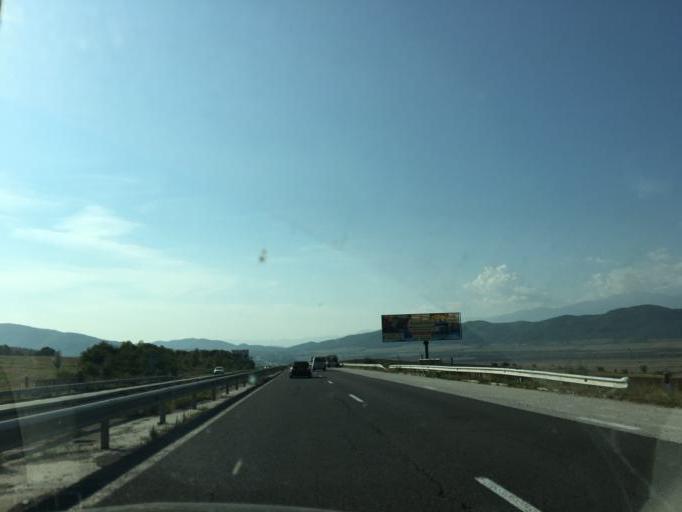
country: BG
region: Sofiya
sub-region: Obshtina Ikhtiman
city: Ikhtiman
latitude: 42.4289
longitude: 23.8534
